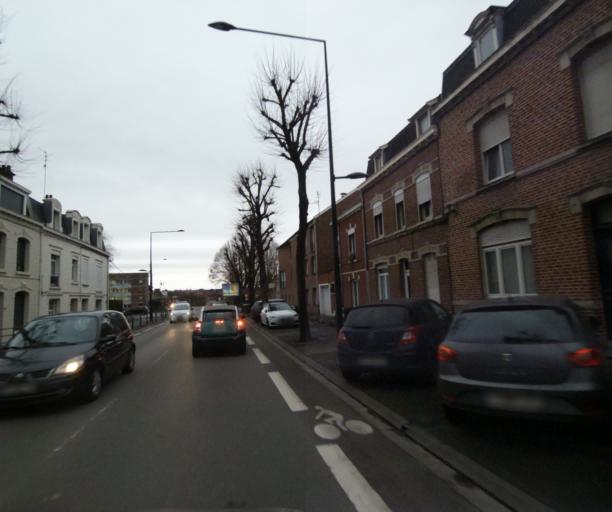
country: FR
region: Nord-Pas-de-Calais
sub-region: Departement du Nord
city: Anzin
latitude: 50.3541
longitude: 3.5091
